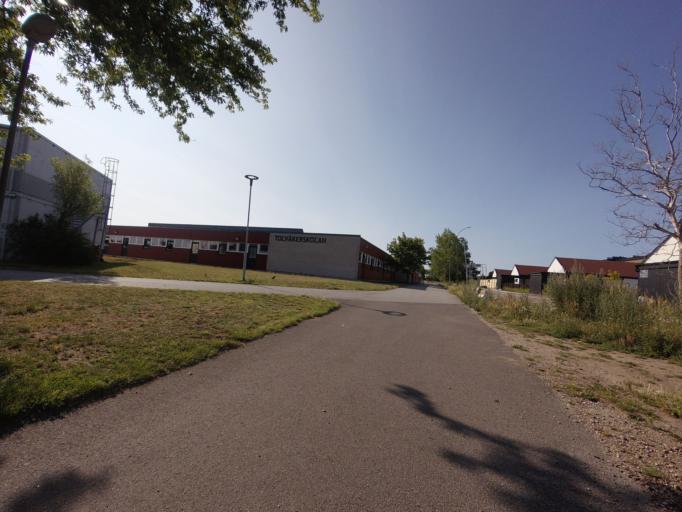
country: SE
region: Skane
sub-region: Kavlinge Kommun
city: Loddekopinge
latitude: 55.7640
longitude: 13.0160
